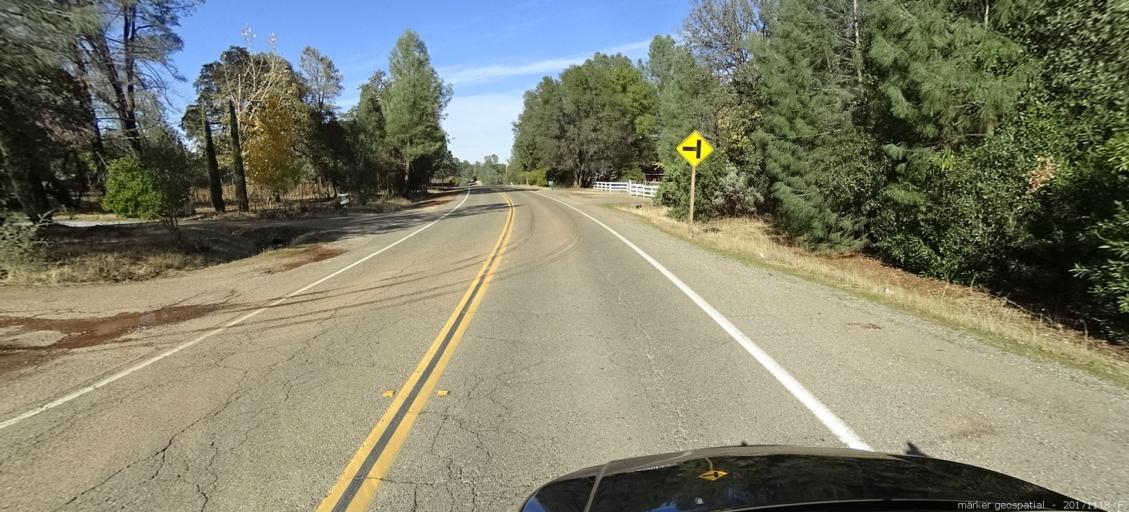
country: US
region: California
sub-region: Shasta County
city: Anderson
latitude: 40.4637
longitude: -122.3966
